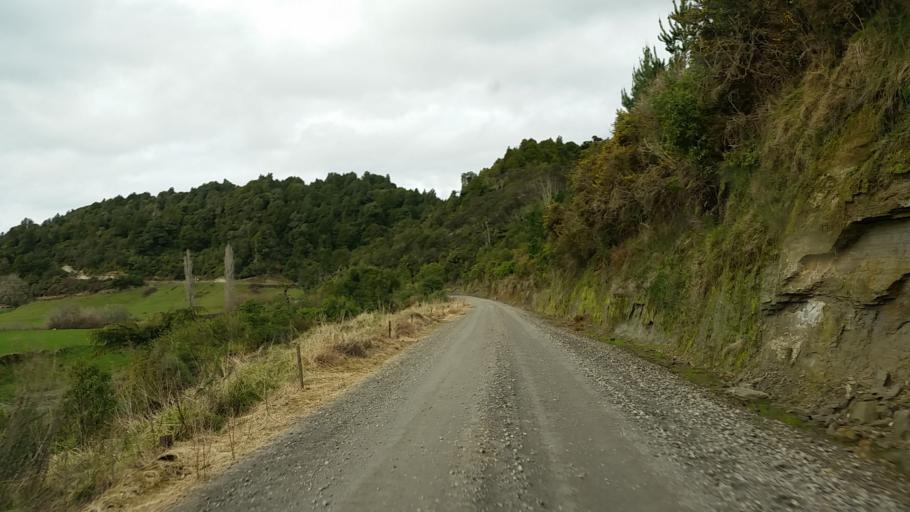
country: NZ
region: Taranaki
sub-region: New Plymouth District
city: Waitara
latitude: -39.1578
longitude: 174.5267
